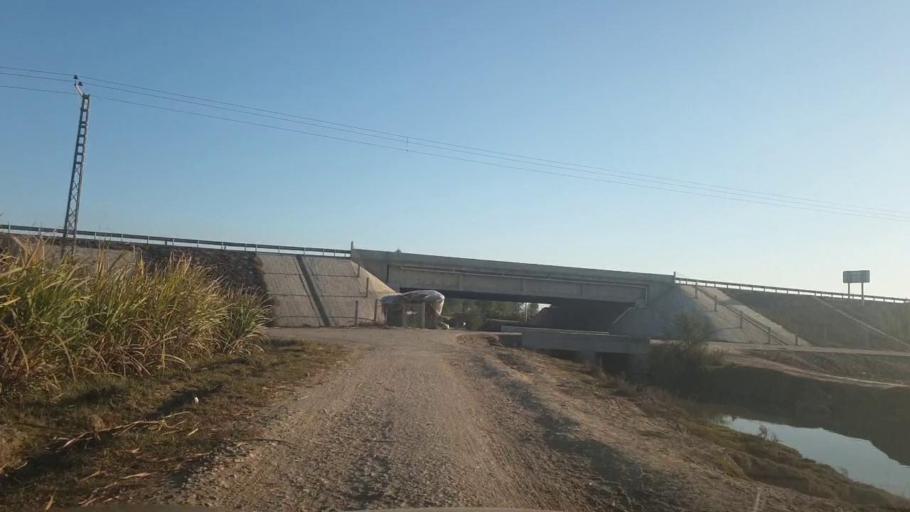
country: PK
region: Sindh
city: Ghotki
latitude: 28.0086
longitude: 69.2692
